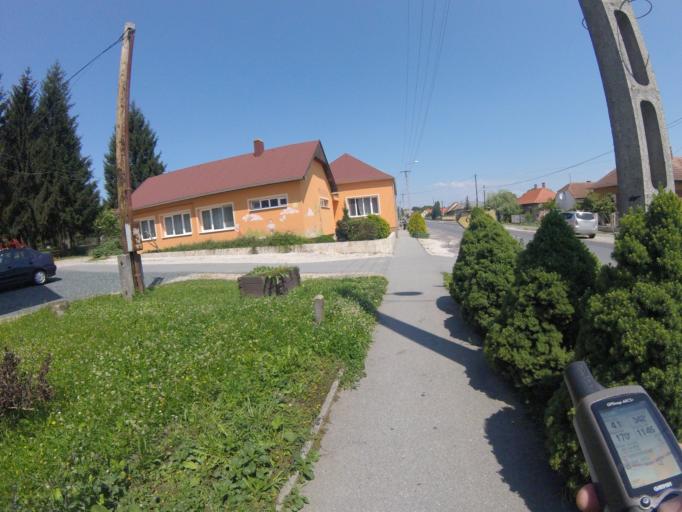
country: HU
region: Zala
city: Lenti
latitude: 46.5567
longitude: 16.5565
